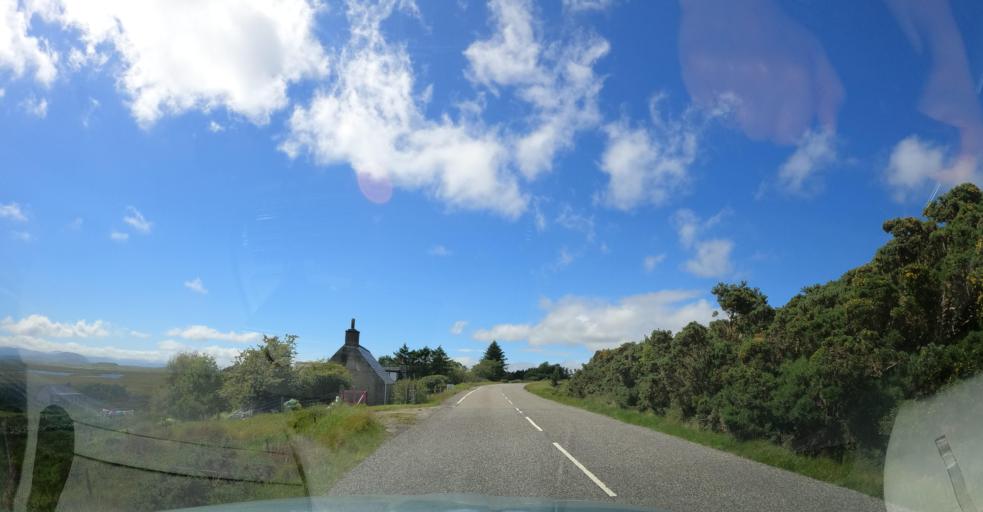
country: GB
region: Scotland
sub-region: Eilean Siar
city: Stornoway
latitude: 58.1658
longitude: -6.5586
